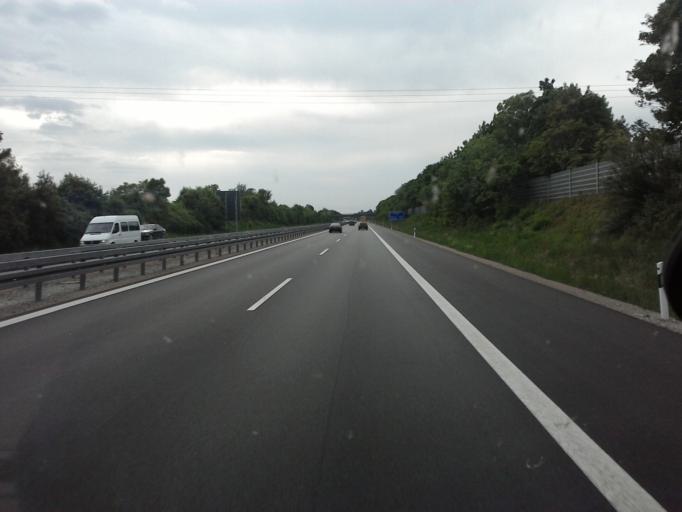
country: DE
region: Bavaria
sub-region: Upper Palatinate
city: Worth an der Donau
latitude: 48.9969
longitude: 12.3987
